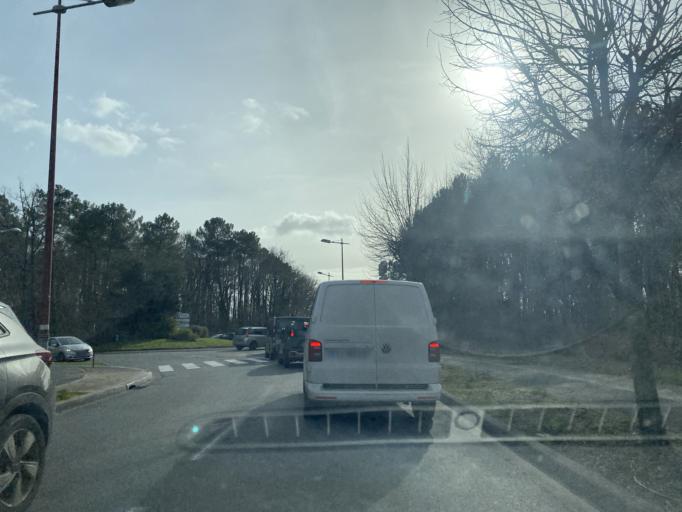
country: FR
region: Aquitaine
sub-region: Departement de la Gironde
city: Le Taillan-Medoc
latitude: 44.9117
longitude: -0.6689
